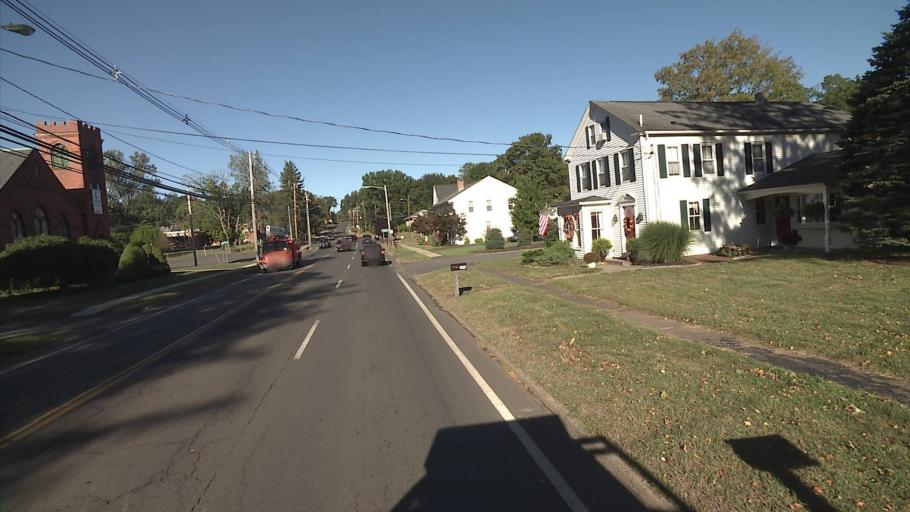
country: US
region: Connecticut
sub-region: New Haven County
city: Wallingford
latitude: 41.4918
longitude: -72.8217
